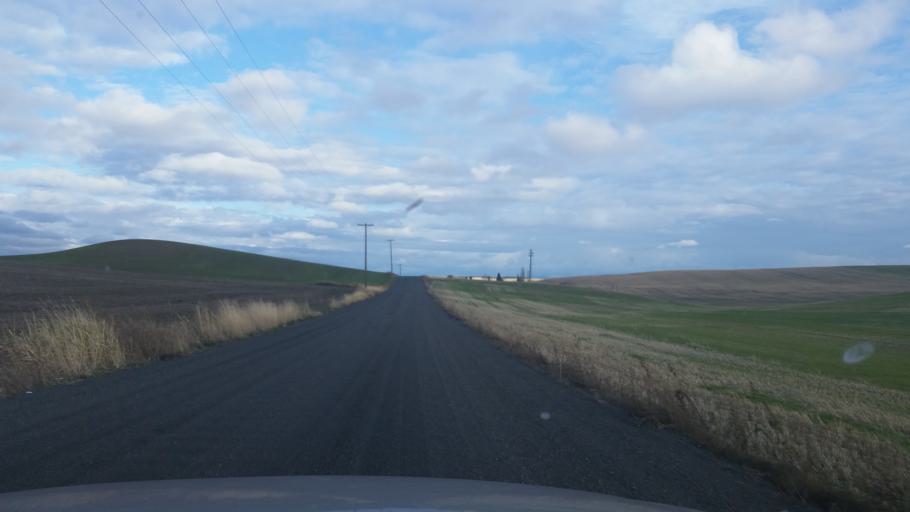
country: US
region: Washington
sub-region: Spokane County
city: Cheney
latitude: 47.4273
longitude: -117.4031
